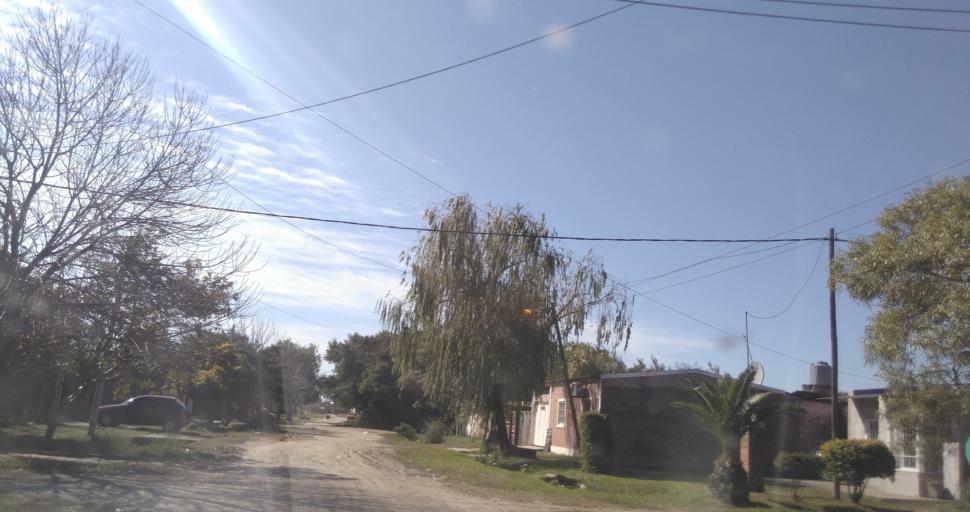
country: AR
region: Chaco
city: Fontana
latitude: -27.4517
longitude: -59.0353
